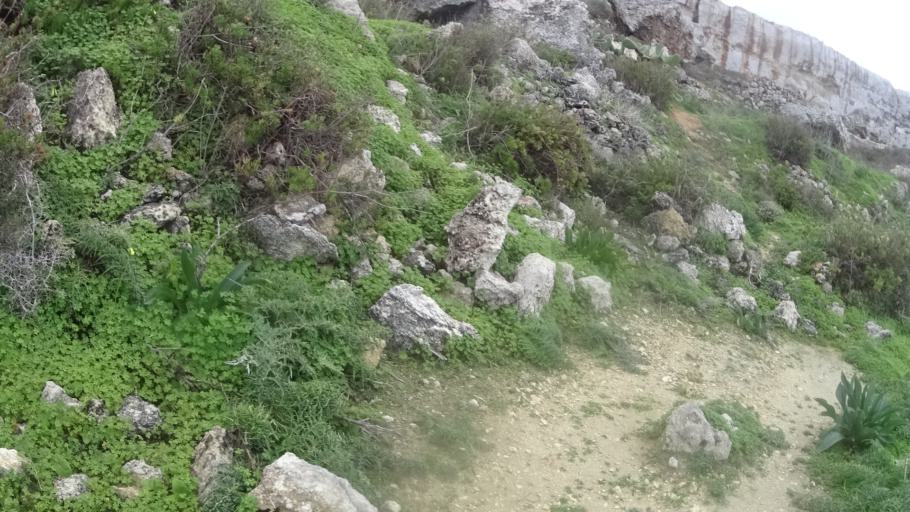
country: MT
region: Il-Mellieha
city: Mellieha
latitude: 35.9780
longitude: 14.3273
